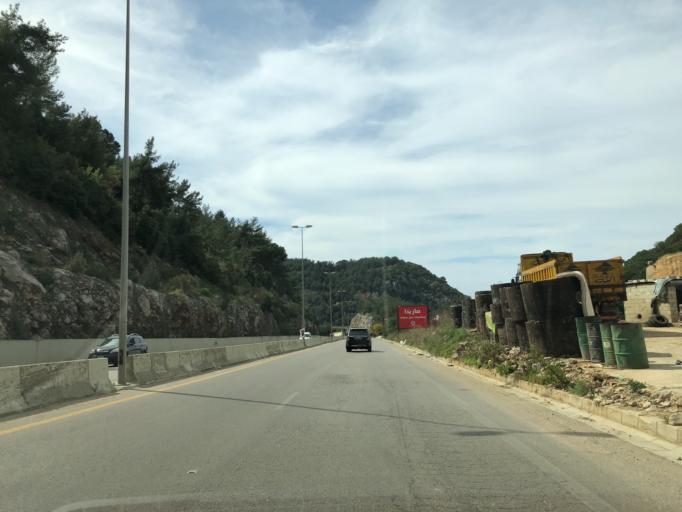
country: LB
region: Mont-Liban
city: Jdaidet el Matn
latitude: 33.8983
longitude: 35.6382
